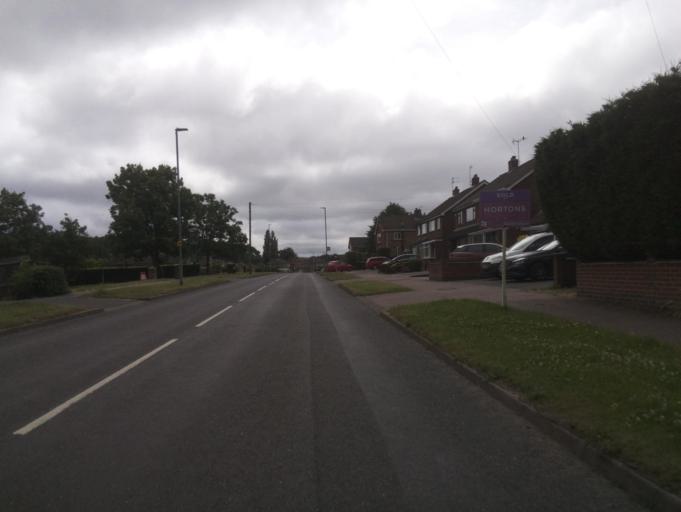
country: GB
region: England
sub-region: Leicestershire
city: Coalville
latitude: 52.7309
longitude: -1.3465
